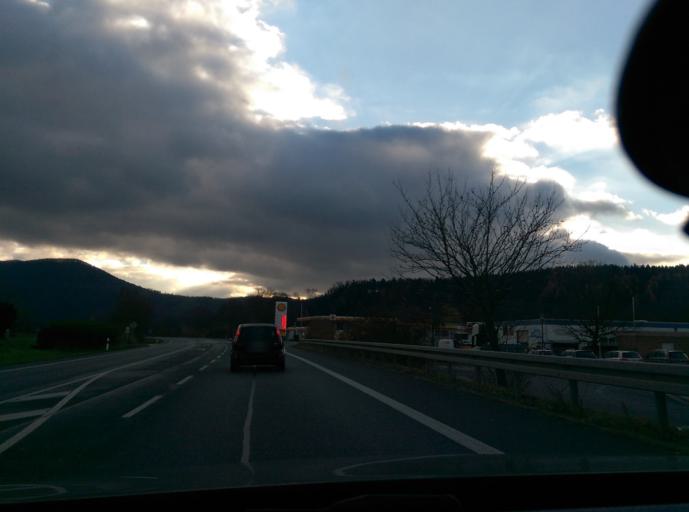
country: DE
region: Hesse
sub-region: Regierungsbezirk Kassel
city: Bad Sooden-Allendorf
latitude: 51.2618
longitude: 9.9801
